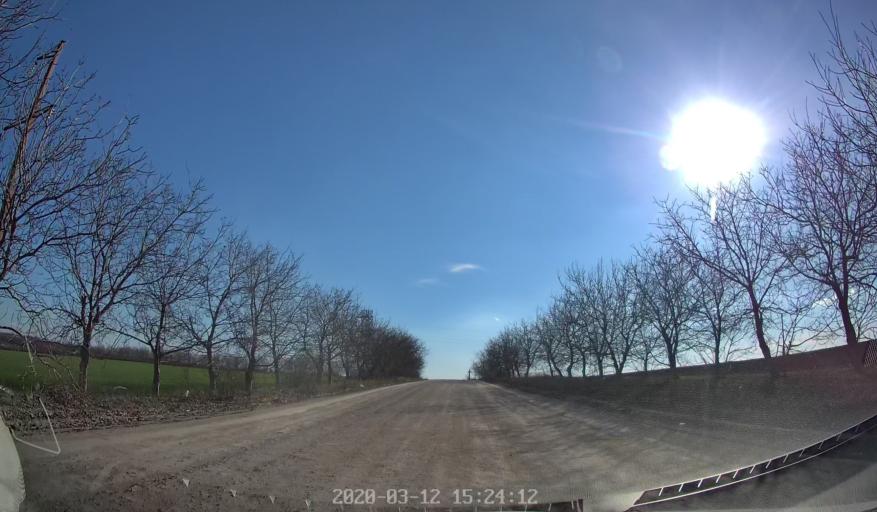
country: MD
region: Chisinau
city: Ciorescu
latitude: 47.1879
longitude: 28.9142
